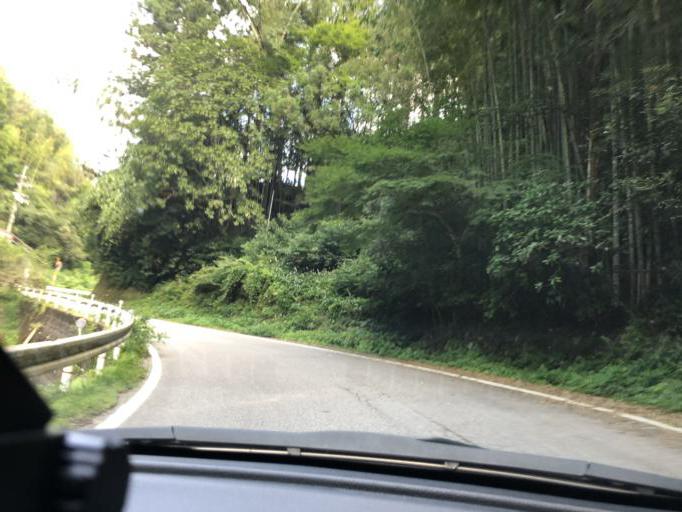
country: JP
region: Kochi
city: Kochi-shi
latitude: 33.6107
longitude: 133.5067
